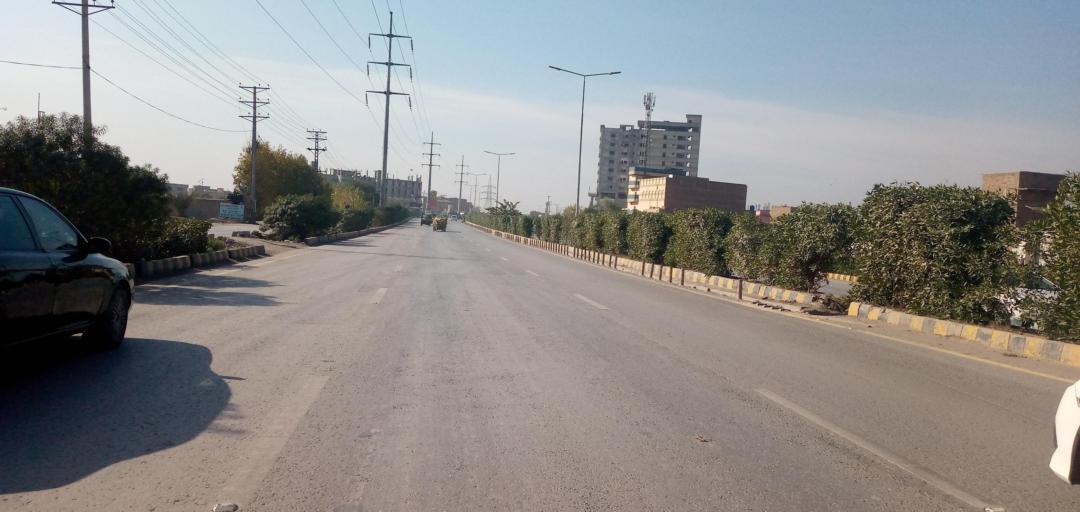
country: PK
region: Khyber Pakhtunkhwa
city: Peshawar
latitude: 33.9652
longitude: 71.5318
